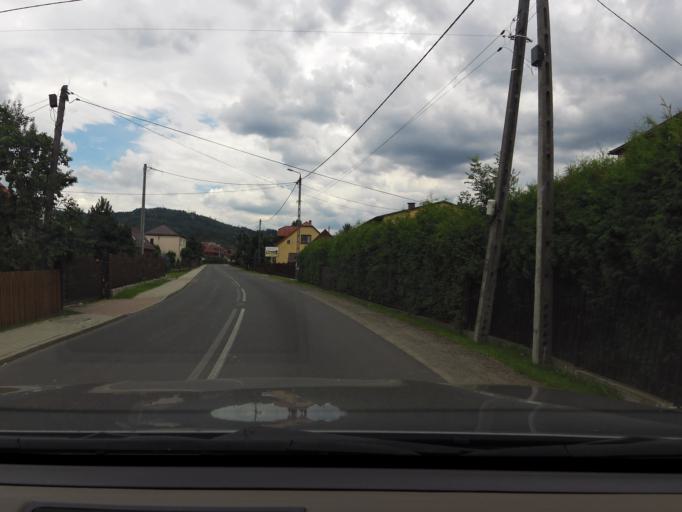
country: PL
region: Silesian Voivodeship
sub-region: Powiat zywiecki
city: Ujsoly
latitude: 49.4838
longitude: 19.1357
